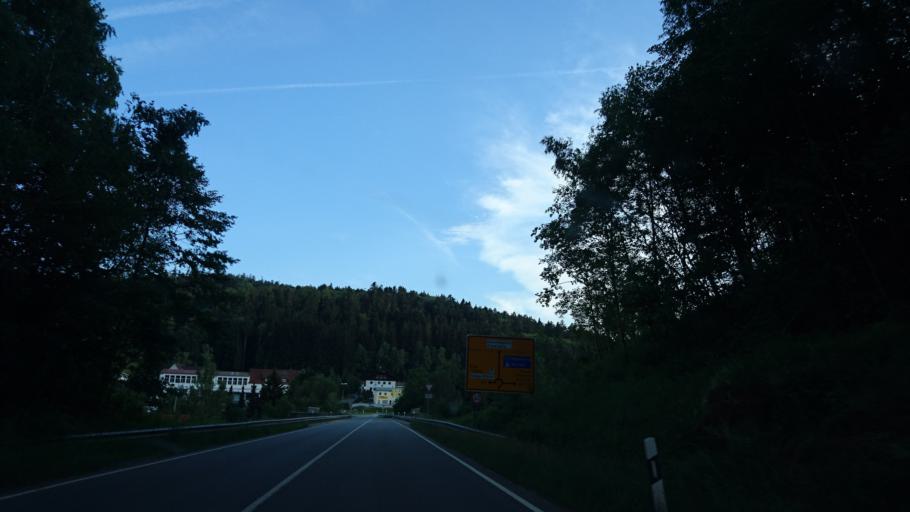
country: DE
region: Bavaria
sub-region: Lower Bavaria
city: Grafenau
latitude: 48.8587
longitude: 13.3851
